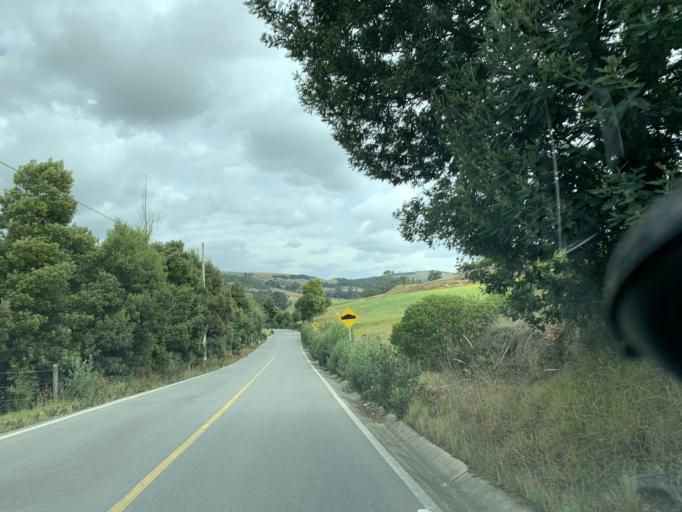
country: CO
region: Boyaca
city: Toca
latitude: 5.5726
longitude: -73.2133
